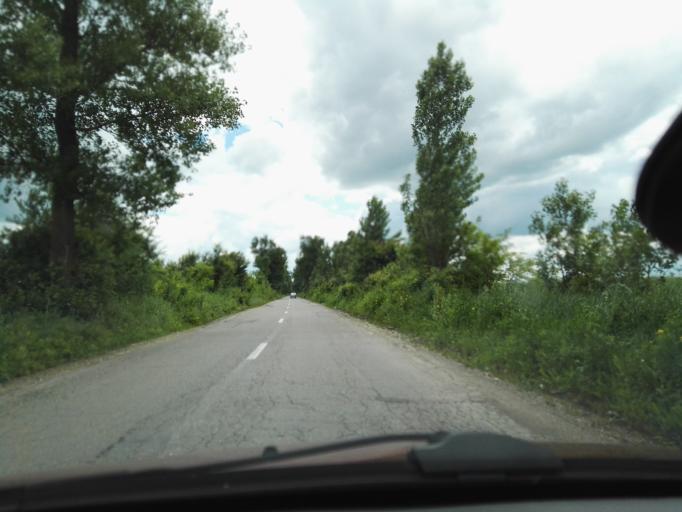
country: RO
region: Giurgiu
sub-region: Comuna Comana
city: Gradistea
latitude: 44.2304
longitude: 26.1312
